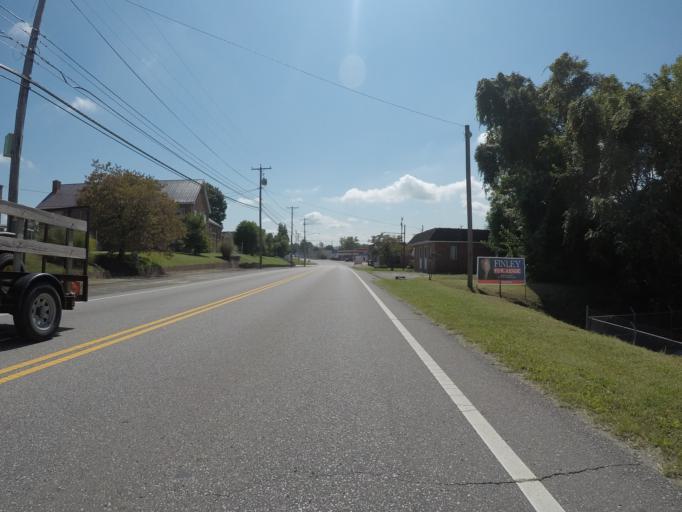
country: US
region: Ohio
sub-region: Lawrence County
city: South Point
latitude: 38.4203
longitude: -82.5886
